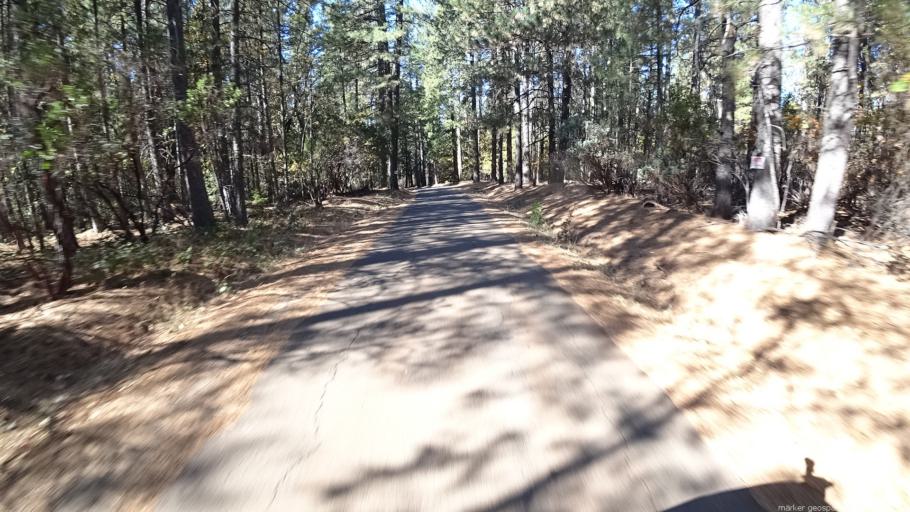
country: US
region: California
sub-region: Shasta County
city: Shingletown
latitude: 40.5204
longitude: -121.9408
